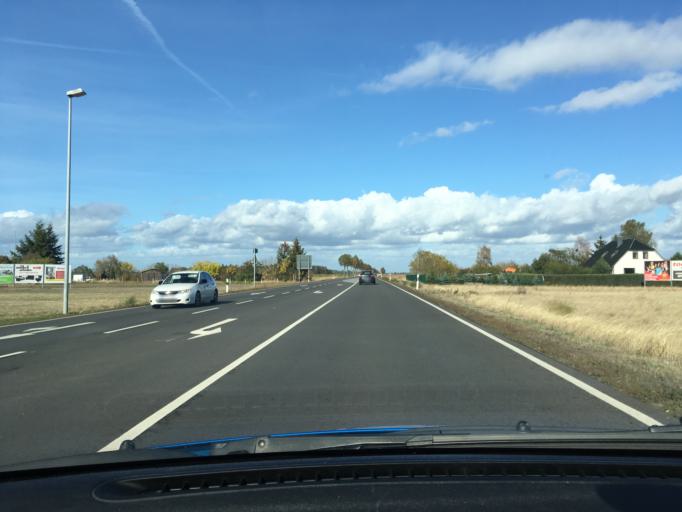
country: DE
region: Saxony-Anhalt
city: Seehausen
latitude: 52.8895
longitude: 11.7309
